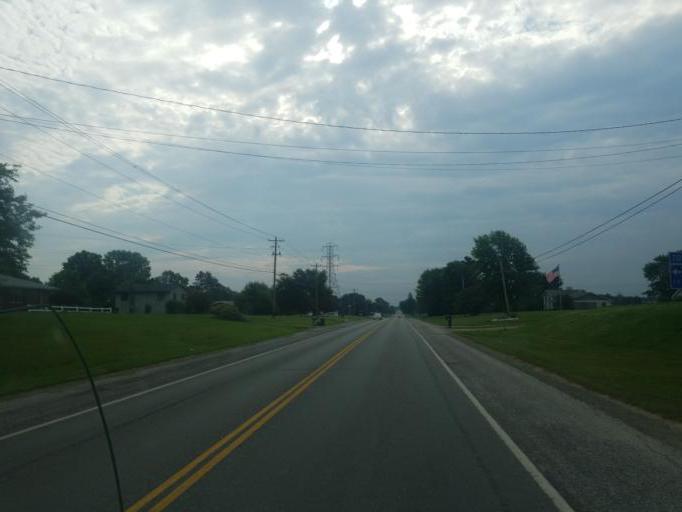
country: US
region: Ohio
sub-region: Wayne County
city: Apple Creek
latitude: 40.7966
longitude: -81.8281
